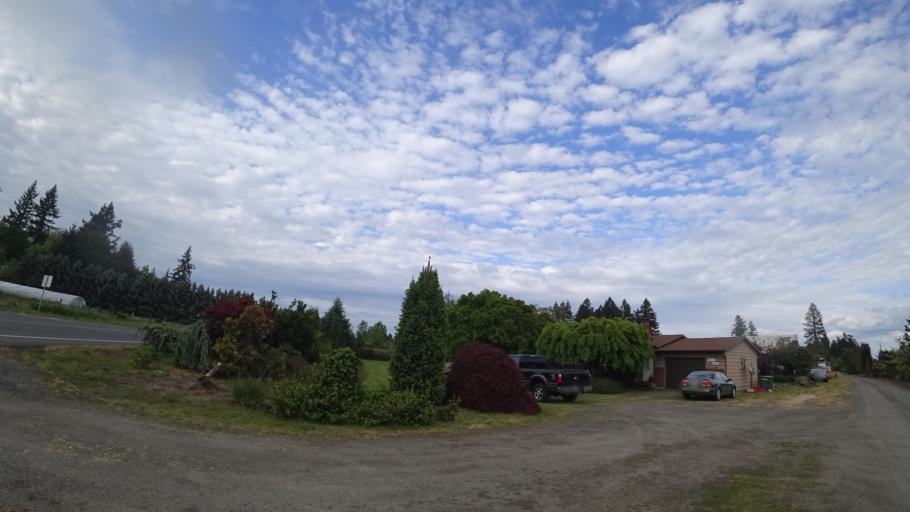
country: US
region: Oregon
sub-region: Washington County
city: Hillsboro
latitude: 45.4802
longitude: -122.9852
